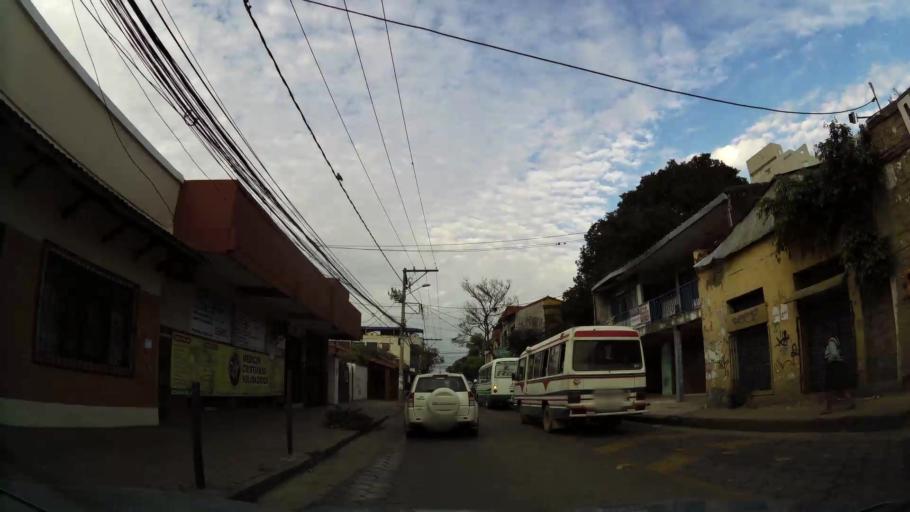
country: BO
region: Santa Cruz
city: Santa Cruz de la Sierra
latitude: -17.7811
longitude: -63.1746
